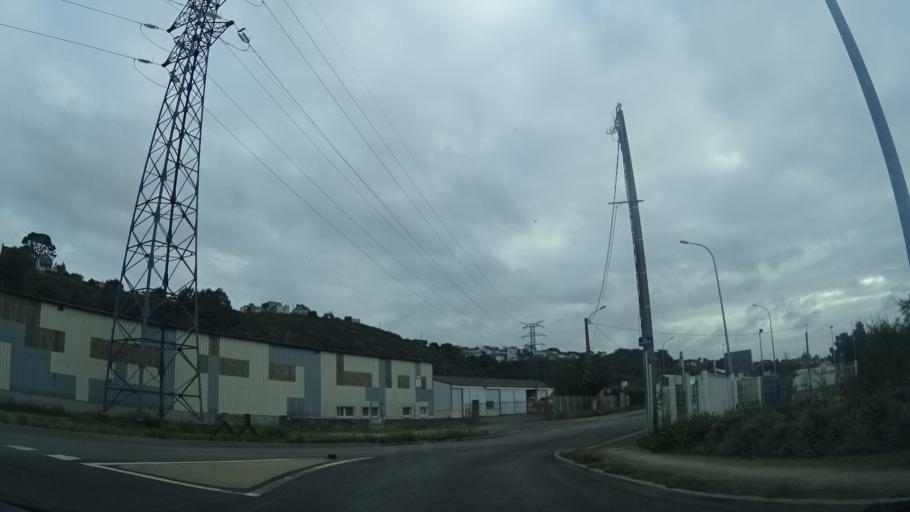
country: FR
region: Brittany
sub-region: Departement du Finistere
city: Brest
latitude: 48.3881
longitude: -4.4599
